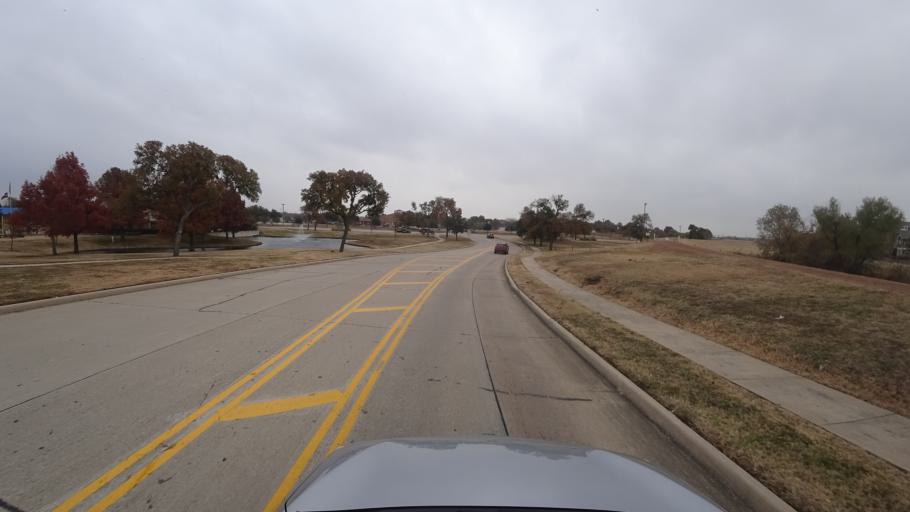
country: US
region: Texas
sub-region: Denton County
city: Lewisville
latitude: 33.0249
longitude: -96.9412
